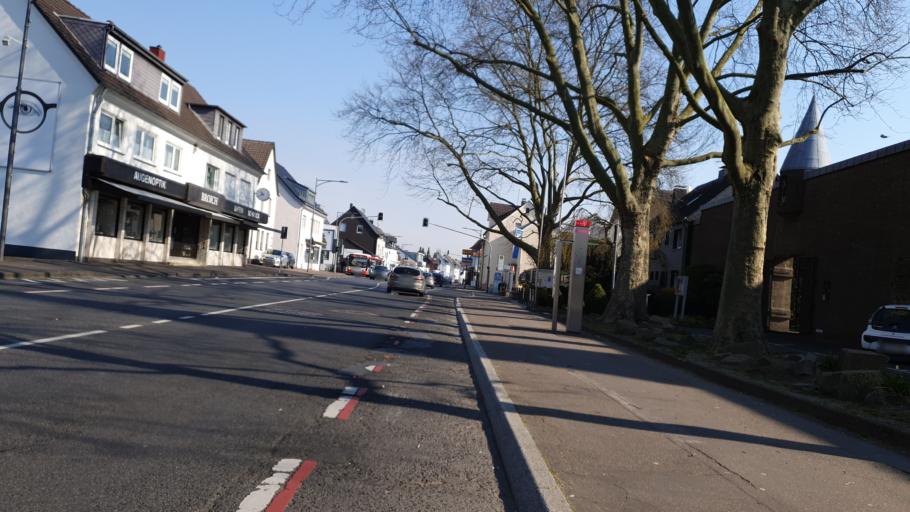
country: DE
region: North Rhine-Westphalia
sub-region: Regierungsbezirk Koln
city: Odenthal
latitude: 51.0154
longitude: 7.0804
